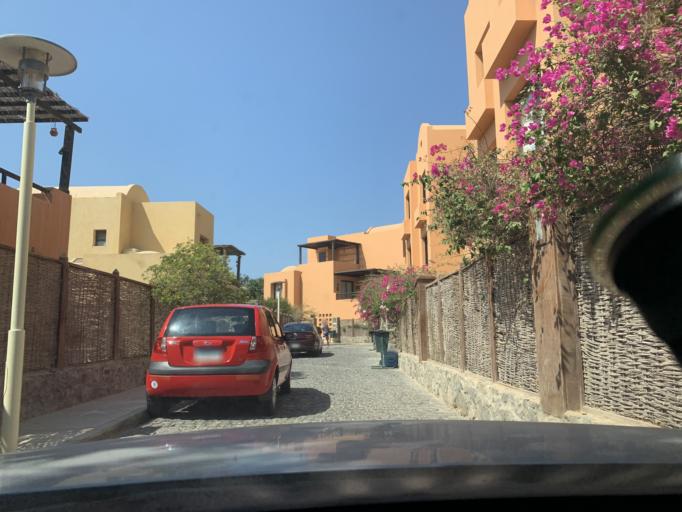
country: EG
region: Red Sea
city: El Gouna
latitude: 27.4014
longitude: 33.6710
